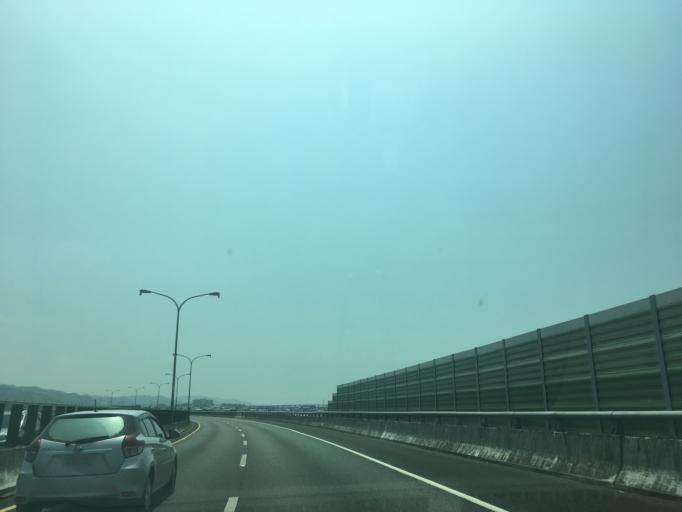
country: TW
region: Taiwan
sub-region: Taichung City
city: Taichung
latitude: 24.0802
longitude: 120.6821
